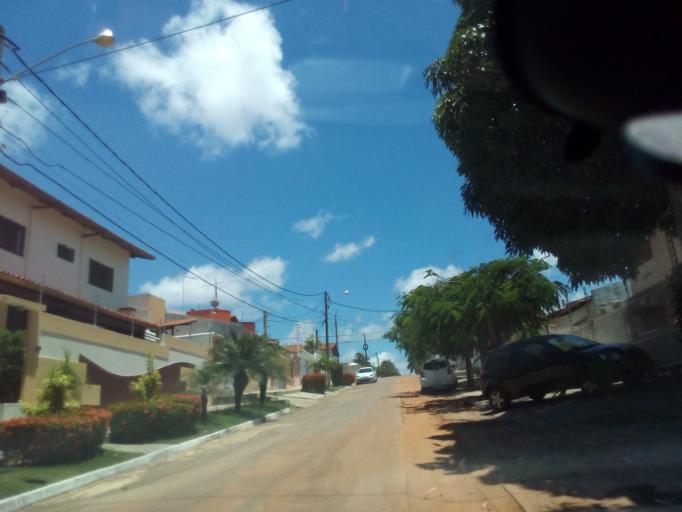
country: BR
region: Rio Grande do Norte
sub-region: Natal
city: Natal
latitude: -5.8453
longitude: -35.1998
